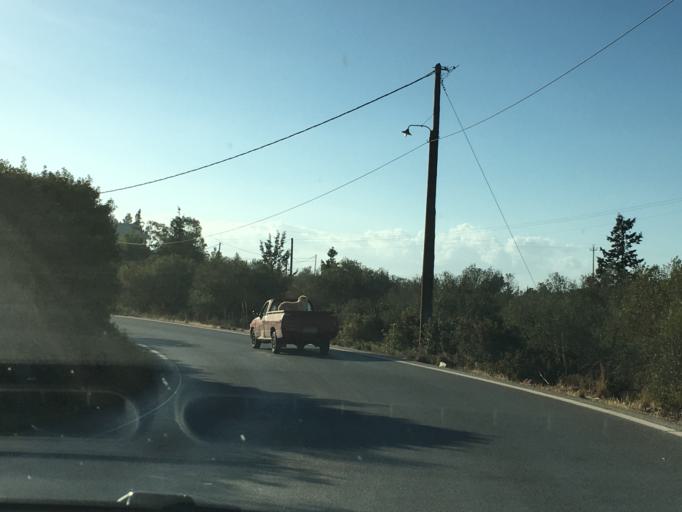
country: GR
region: Crete
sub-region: Nomos Chanias
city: Pithari
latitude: 35.5389
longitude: 24.0995
